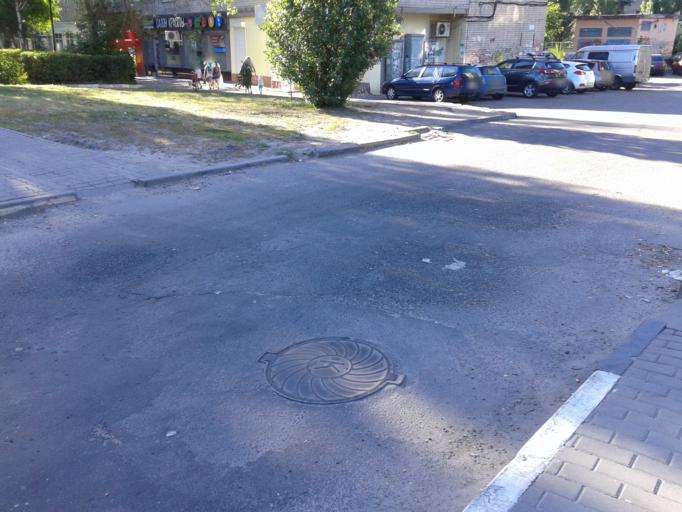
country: RU
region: Voronezj
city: Pridonskoy
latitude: 51.6547
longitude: 39.1248
